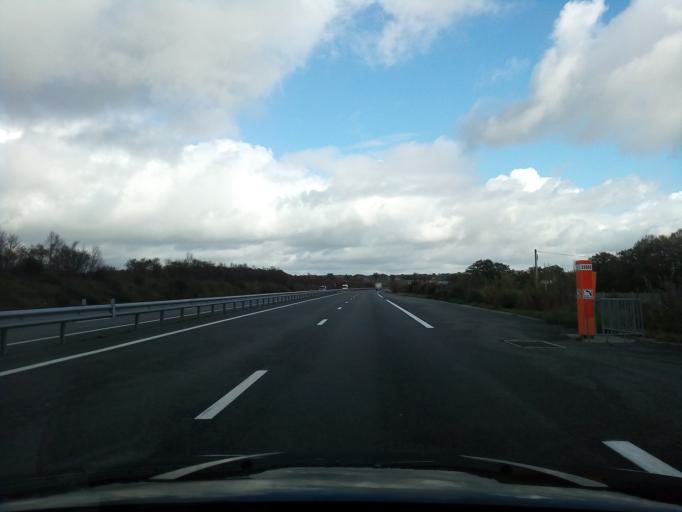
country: FR
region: Limousin
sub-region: Departement de la Creuse
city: Gouzon
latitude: 46.2140
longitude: 2.2819
